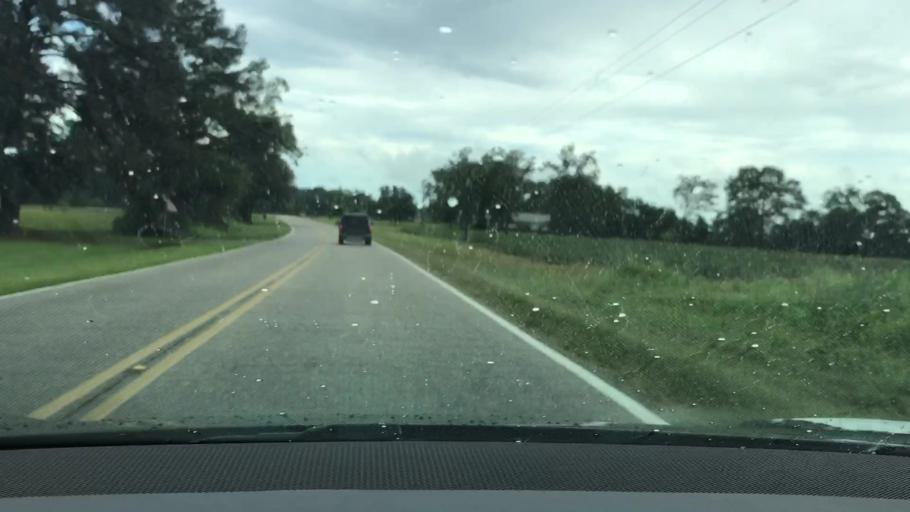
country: US
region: Alabama
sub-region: Geneva County
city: Samson
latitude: 31.1225
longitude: -86.1251
